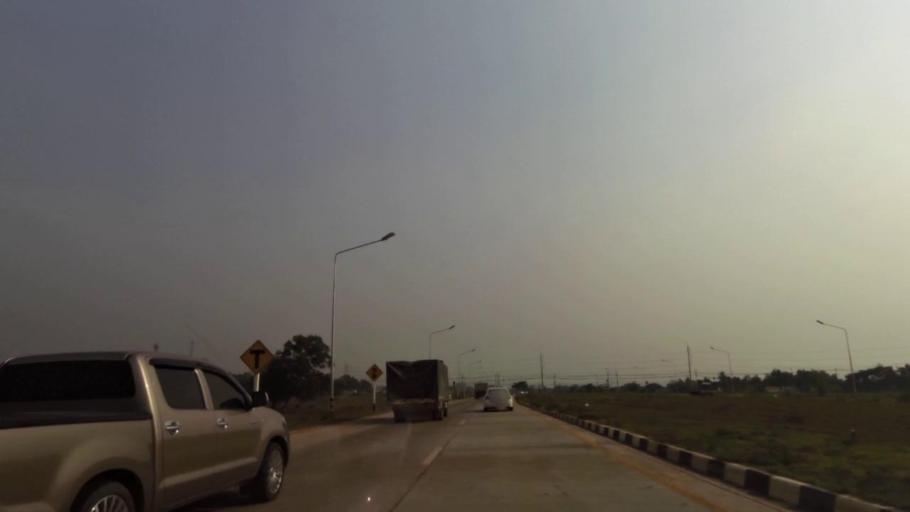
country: TH
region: Rayong
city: Klaeng
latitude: 12.7879
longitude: 101.6766
